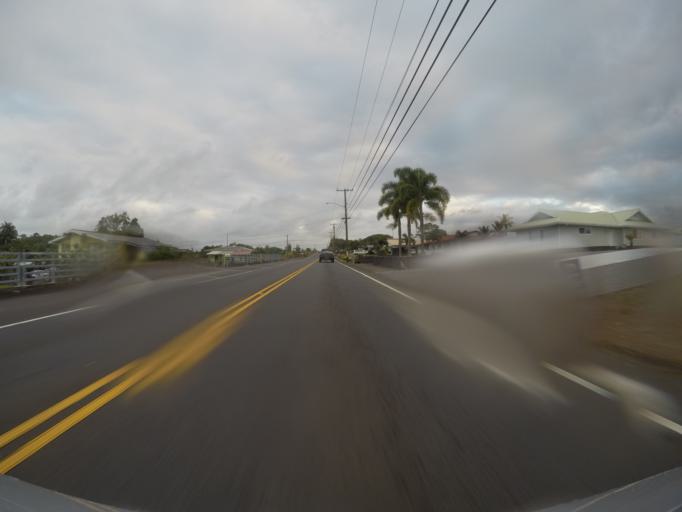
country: US
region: Hawaii
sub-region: Hawaii County
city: Hilo
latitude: 19.6856
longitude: -155.0899
